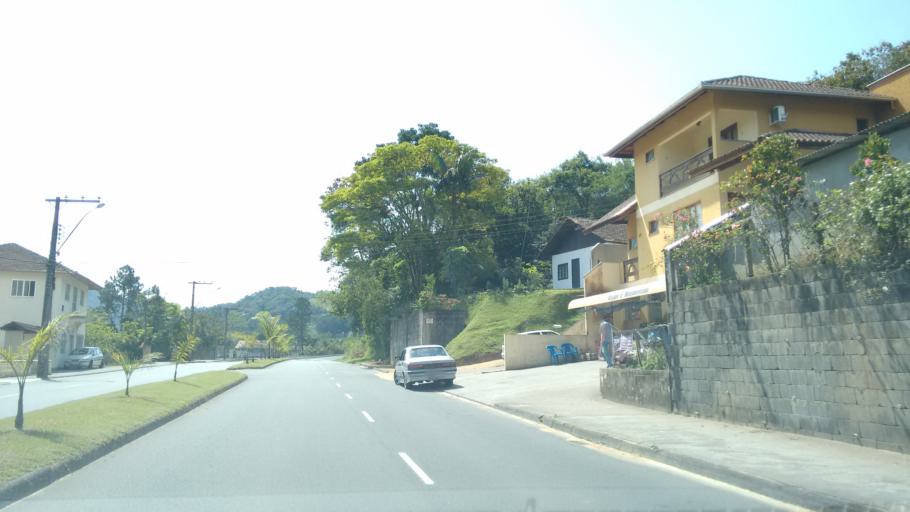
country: BR
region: Santa Catarina
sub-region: Pomerode
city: Pomerode
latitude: -26.7256
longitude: -49.1795
